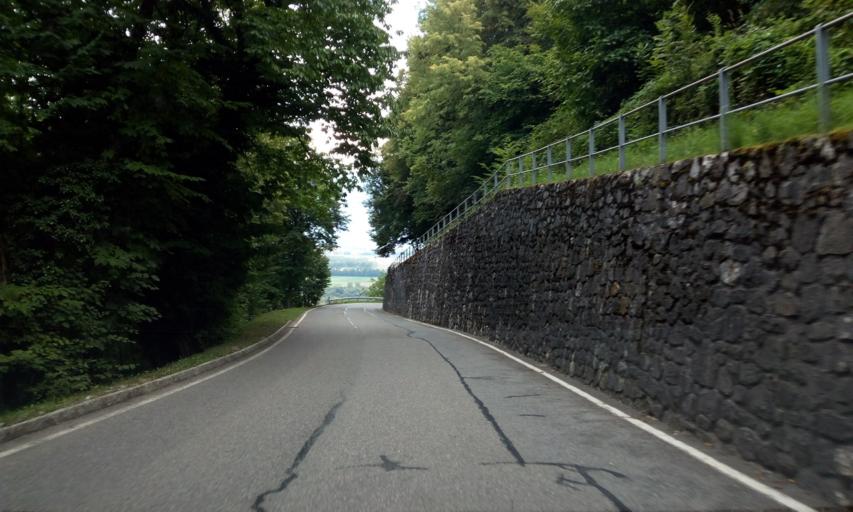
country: CH
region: Valais
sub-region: Monthey District
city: Vionnaz
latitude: 46.3101
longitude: 6.8948
